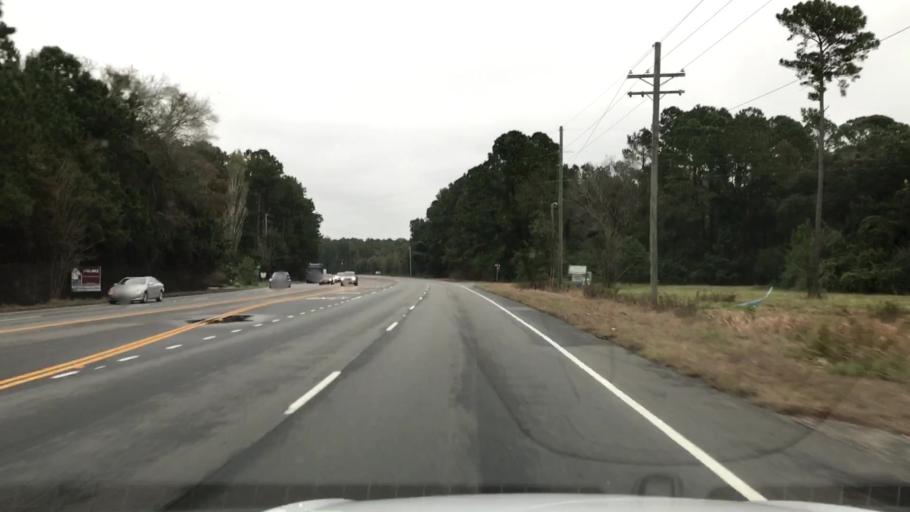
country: US
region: South Carolina
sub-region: Charleston County
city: Awendaw
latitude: 33.0994
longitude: -79.4697
